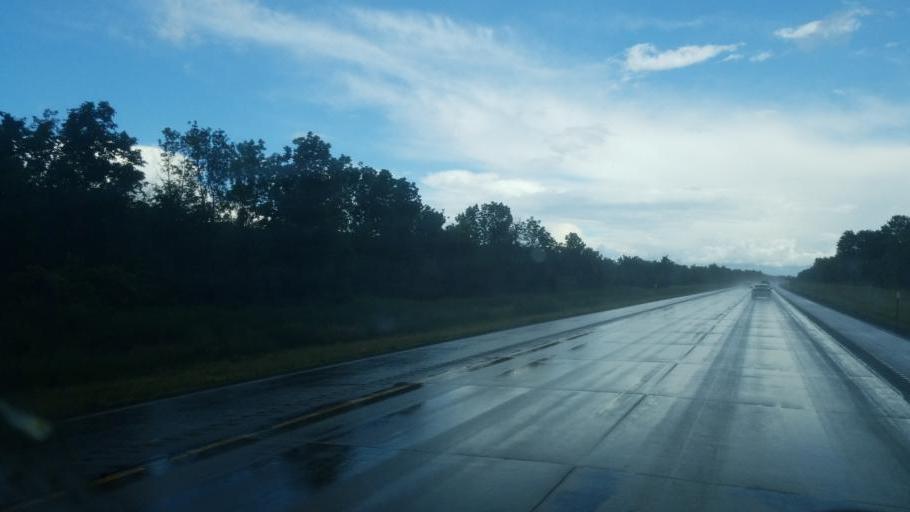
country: US
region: New York
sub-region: Erie County
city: Wanakah
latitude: 42.7009
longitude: -78.9210
